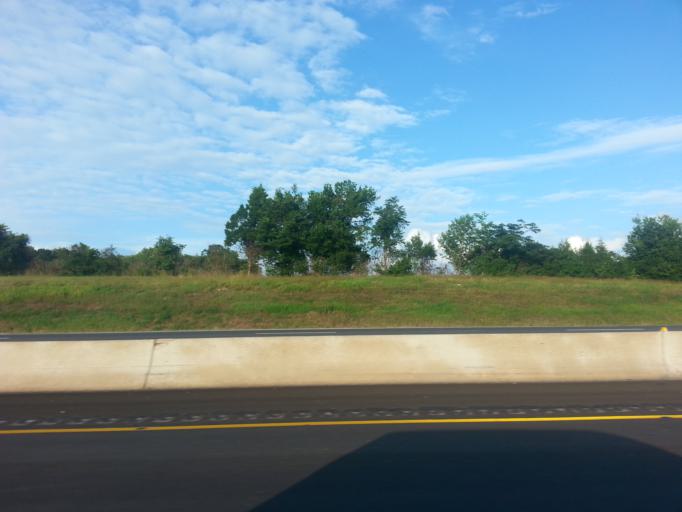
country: US
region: Kentucky
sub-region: Madison County
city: Richmond
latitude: 37.6836
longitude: -84.3136
